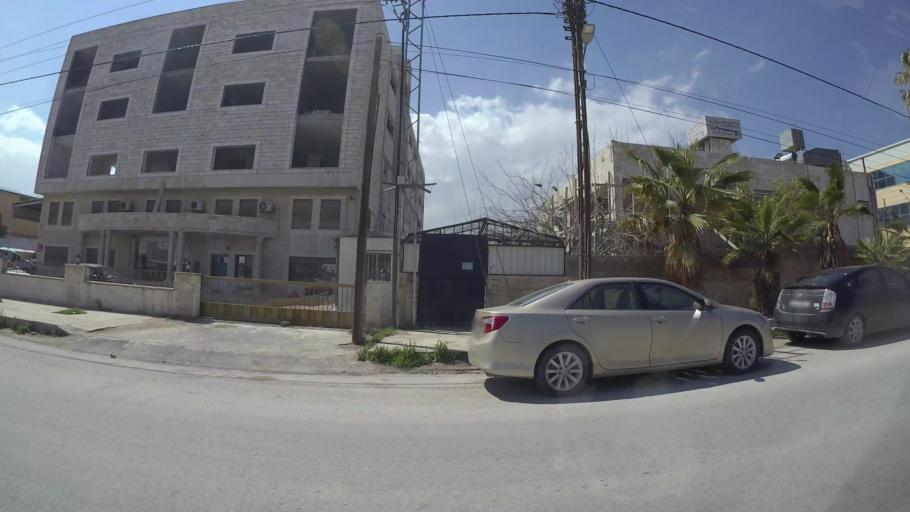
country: JO
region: Zarqa
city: Russeifa
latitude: 31.9944
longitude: 36.0116
